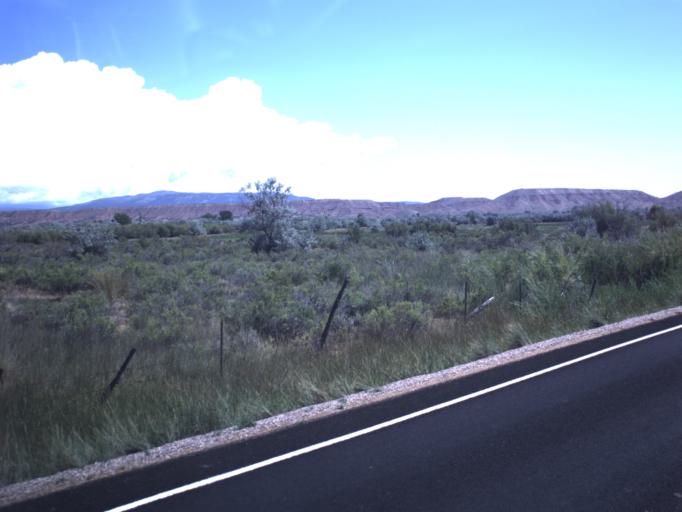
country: US
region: Utah
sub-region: Duchesne County
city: Roosevelt
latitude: 40.4037
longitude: -109.8454
